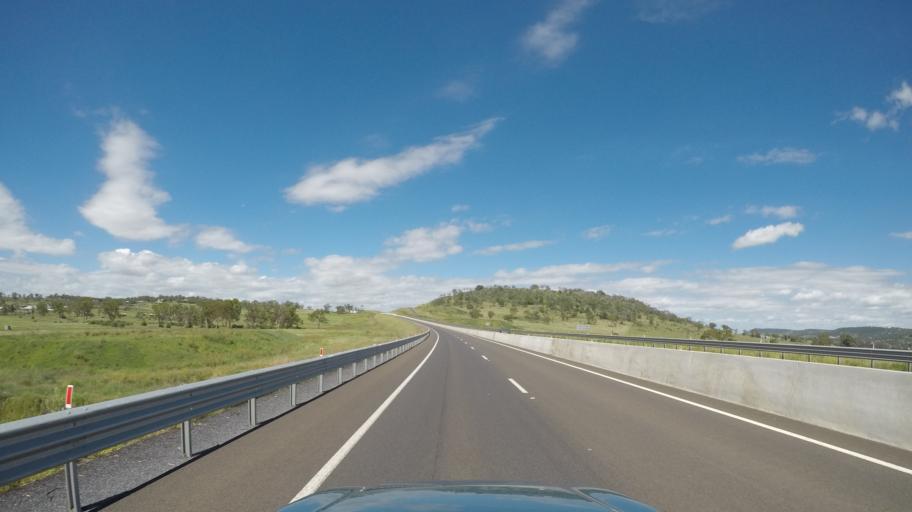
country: AU
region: Queensland
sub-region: Toowoomba
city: Wilsonton Heights
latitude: -27.5074
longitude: 151.9051
